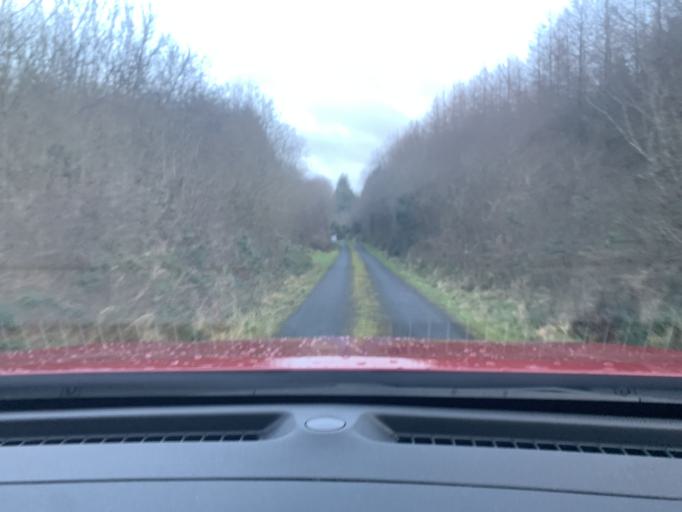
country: IE
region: Connaught
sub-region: Sligo
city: Ballymote
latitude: 53.9896
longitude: -8.4461
